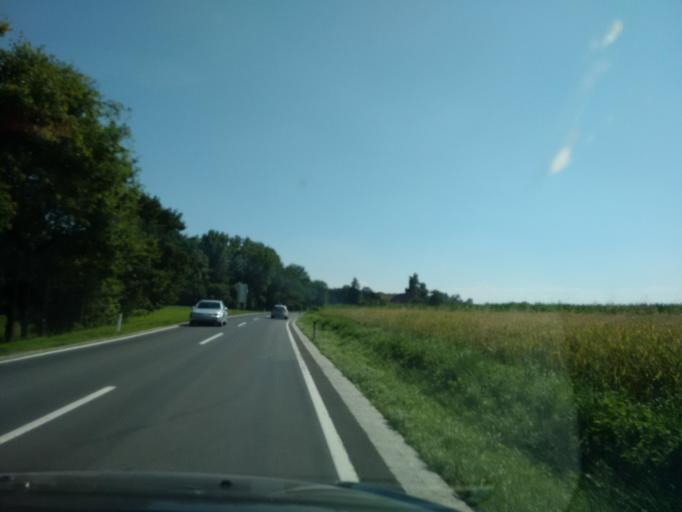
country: AT
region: Upper Austria
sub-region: Wels-Land
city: Buchkirchen
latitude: 48.2753
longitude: 13.9949
